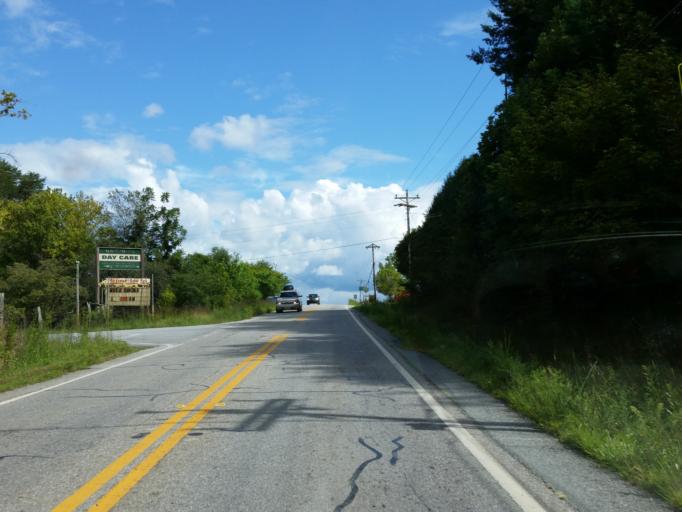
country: US
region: Georgia
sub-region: Fannin County
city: Blue Ridge
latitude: 34.8816
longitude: -84.2501
